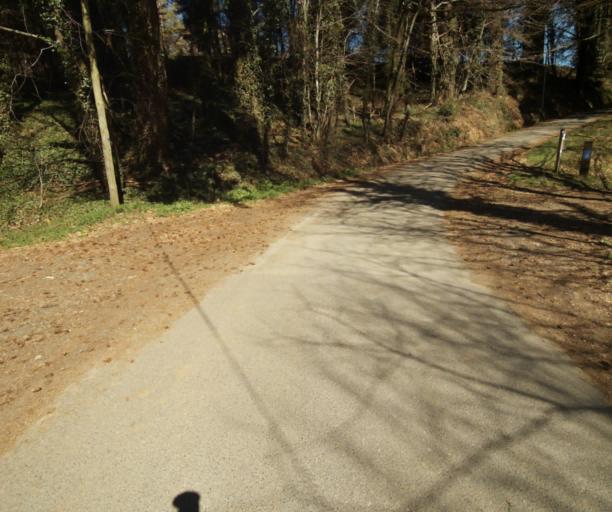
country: FR
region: Limousin
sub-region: Departement de la Correze
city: Saint-Clement
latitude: 45.3133
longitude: 1.7115
